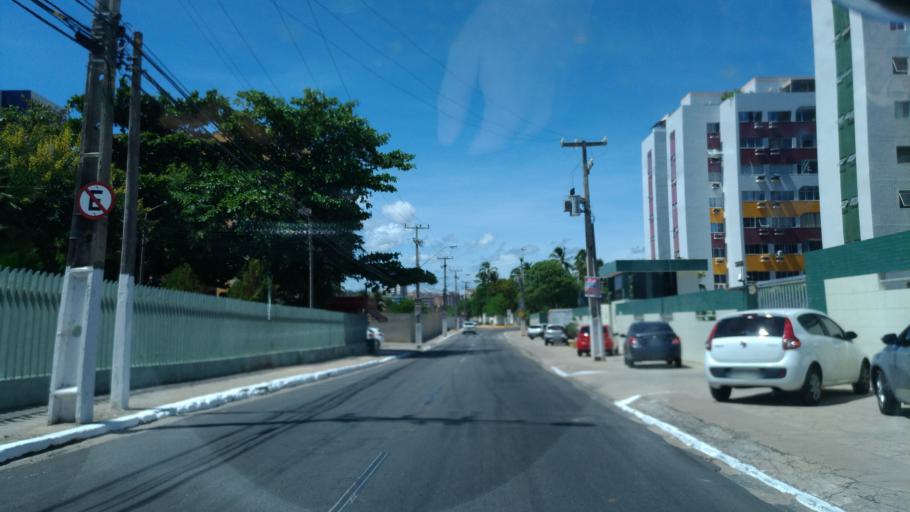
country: BR
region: Alagoas
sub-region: Maceio
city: Maceio
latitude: -9.6409
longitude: -35.7004
